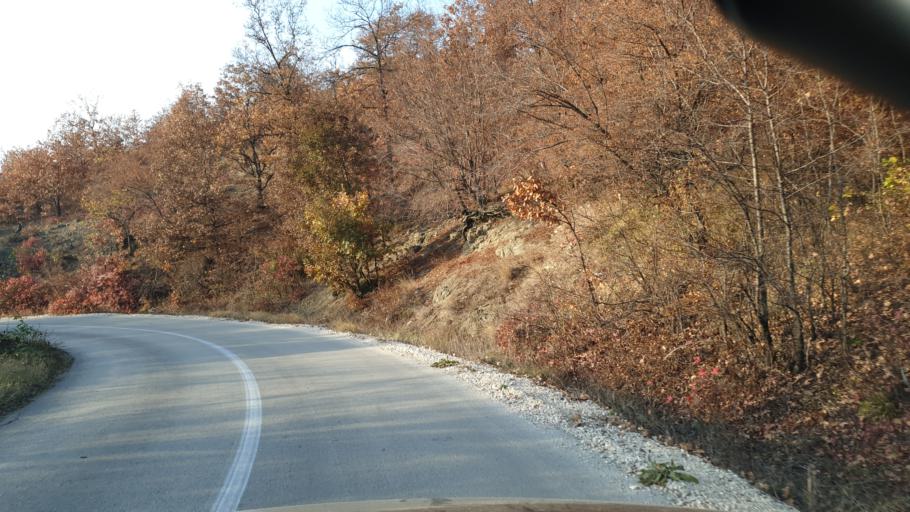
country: RS
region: Central Serbia
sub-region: Borski Okrug
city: Bor
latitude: 44.0471
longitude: 22.0796
